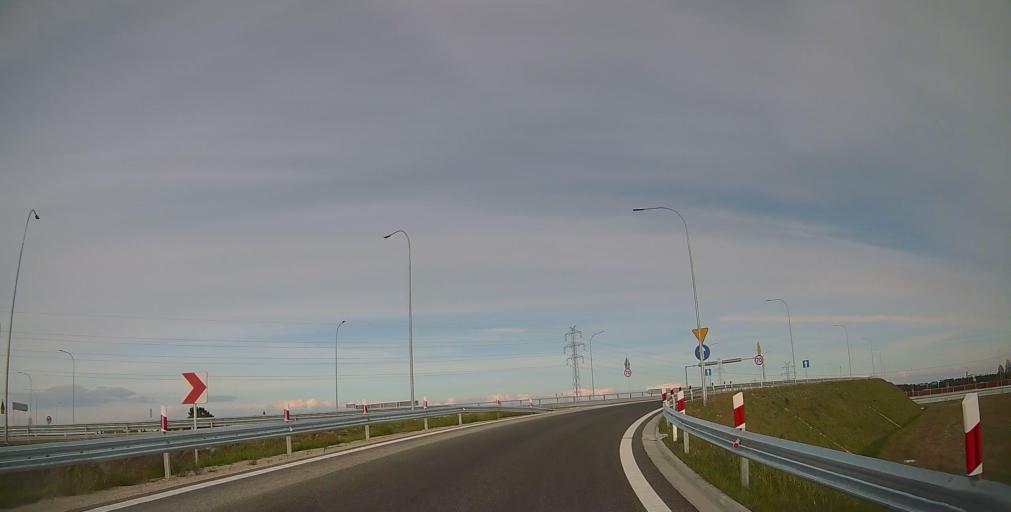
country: PL
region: Masovian Voivodeship
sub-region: Powiat piaseczynski
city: Lesznowola
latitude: 52.0884
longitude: 20.9661
